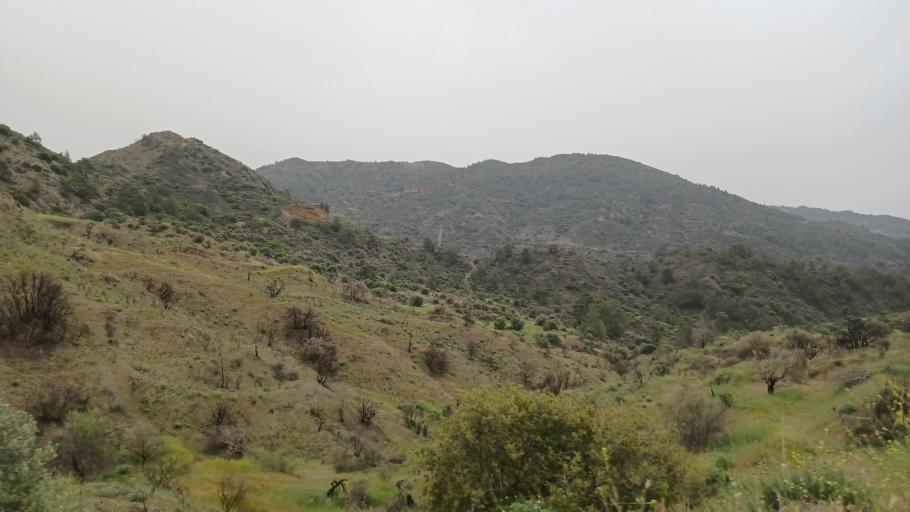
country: CY
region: Limassol
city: Parekklisha
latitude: 34.8374
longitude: 33.1309
